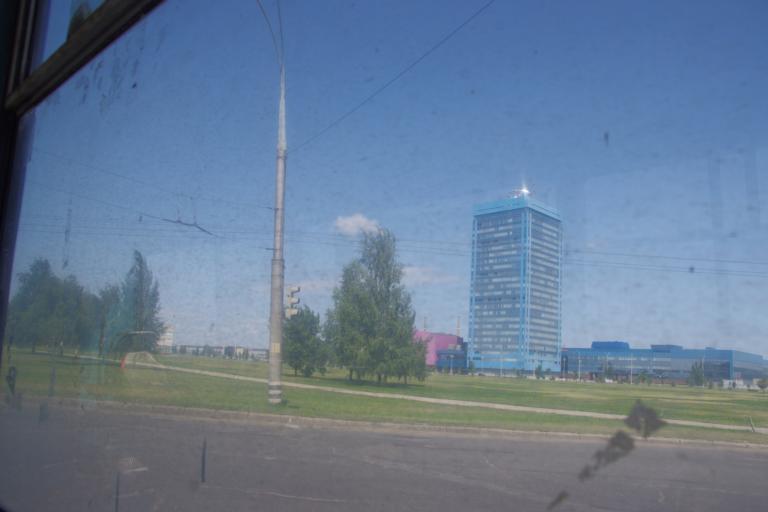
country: RU
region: Samara
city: Tol'yatti
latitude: 53.5530
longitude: 49.2666
